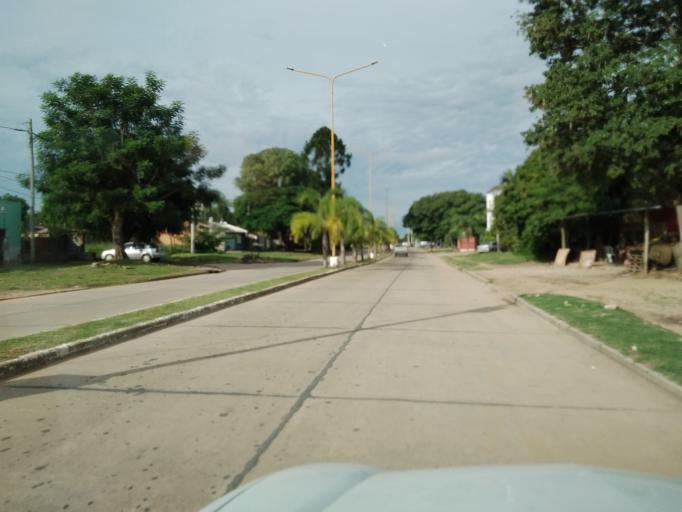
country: AR
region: Corrientes
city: Corrientes
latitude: -27.4609
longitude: -58.7789
